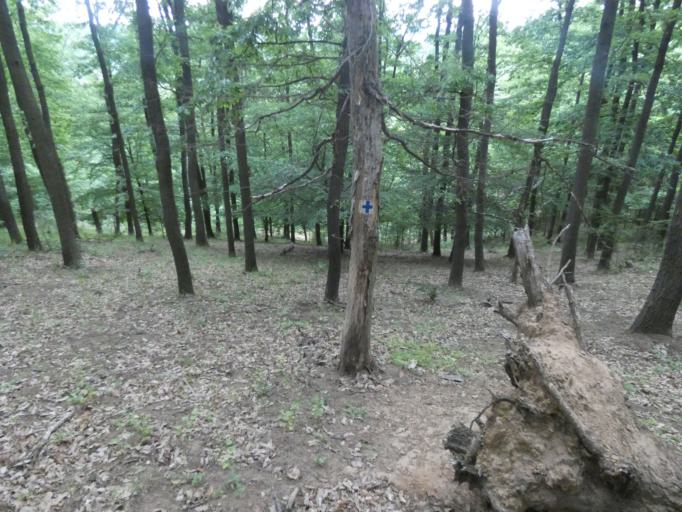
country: HU
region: Heves
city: Petervasara
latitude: 48.1189
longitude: 20.1056
